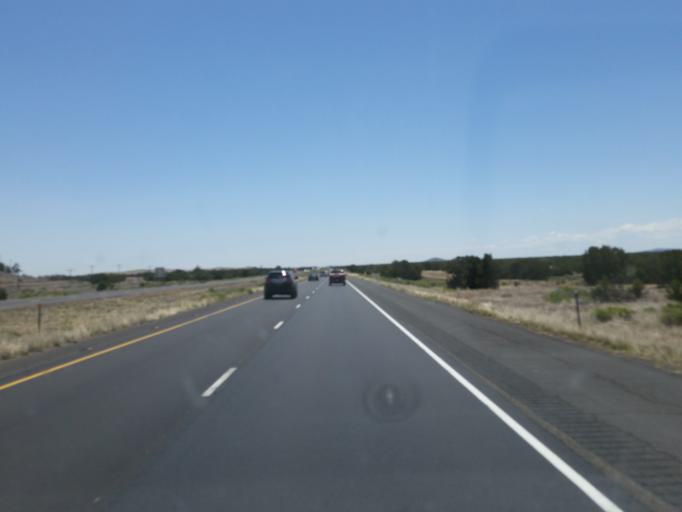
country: US
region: Arizona
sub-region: Coconino County
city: Flagstaff
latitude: 35.1945
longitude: -111.3898
